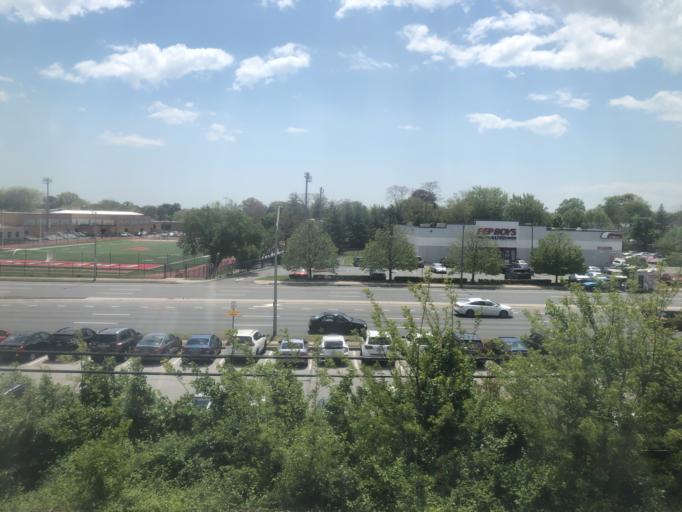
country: US
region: New York
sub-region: Nassau County
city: Baldwin
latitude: 40.6567
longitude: -73.6038
